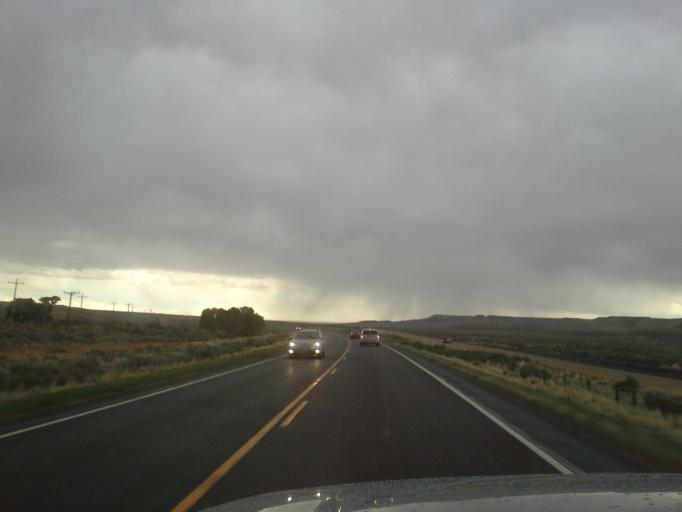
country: US
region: Wyoming
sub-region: Park County
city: Powell
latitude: 45.0490
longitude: -108.6535
